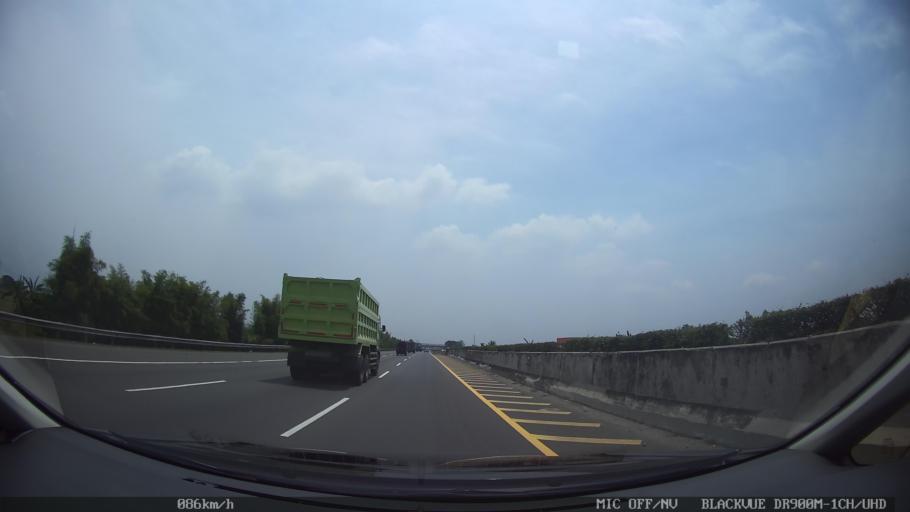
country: ID
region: West Java
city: Kresek
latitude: -6.1771
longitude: 106.3726
